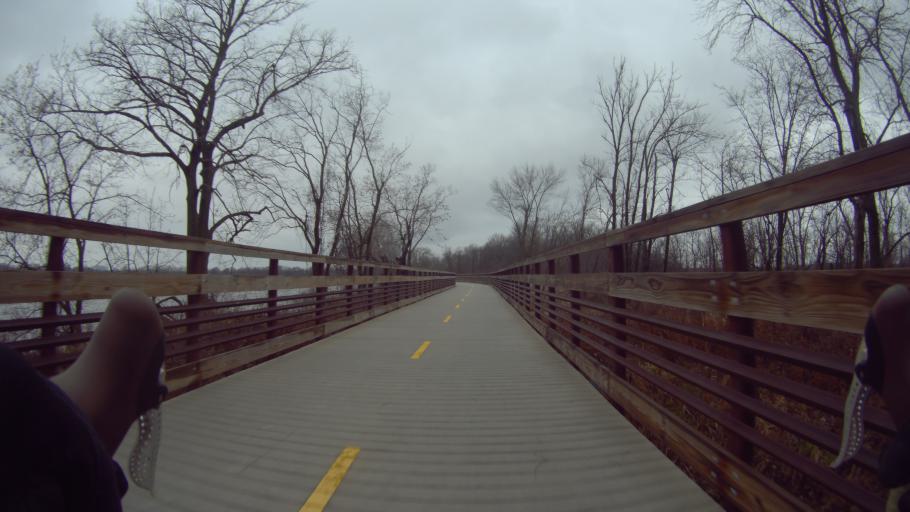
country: US
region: Wisconsin
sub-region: Dane County
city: McFarland
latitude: 43.0298
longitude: -89.3129
